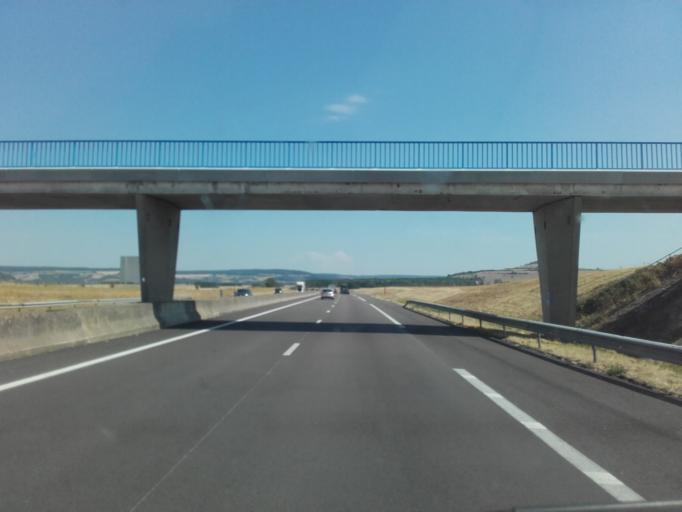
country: FR
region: Bourgogne
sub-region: Departement de la Cote-d'Or
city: Vitteaux
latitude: 47.3597
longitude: 4.4260
